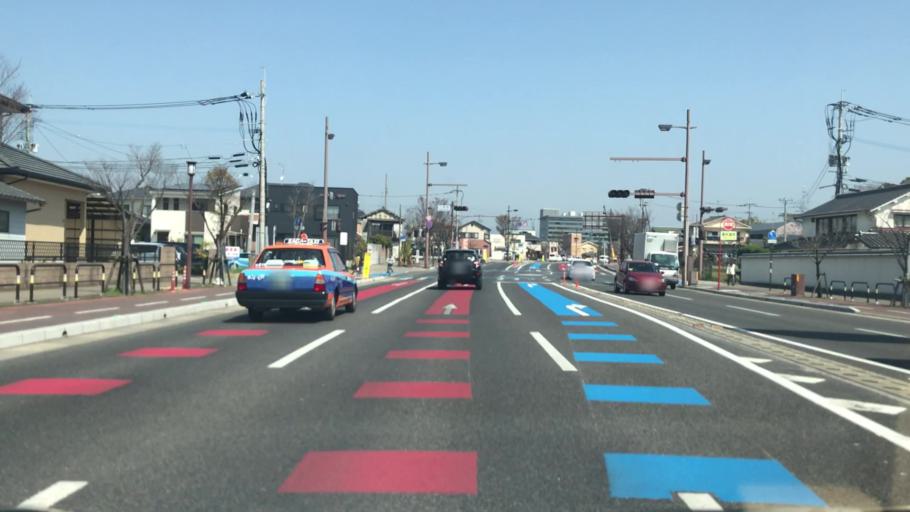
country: JP
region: Saga Prefecture
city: Saga-shi
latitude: 33.2514
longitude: 130.2922
